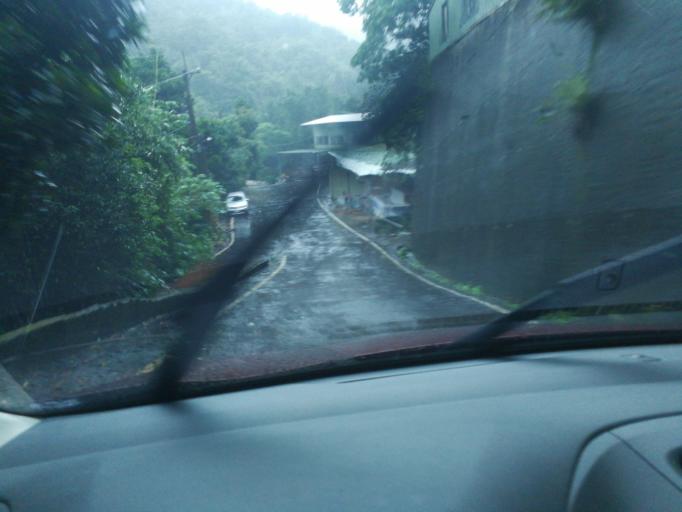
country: TW
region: Taipei
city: Taipei
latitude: 25.1106
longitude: 121.6257
